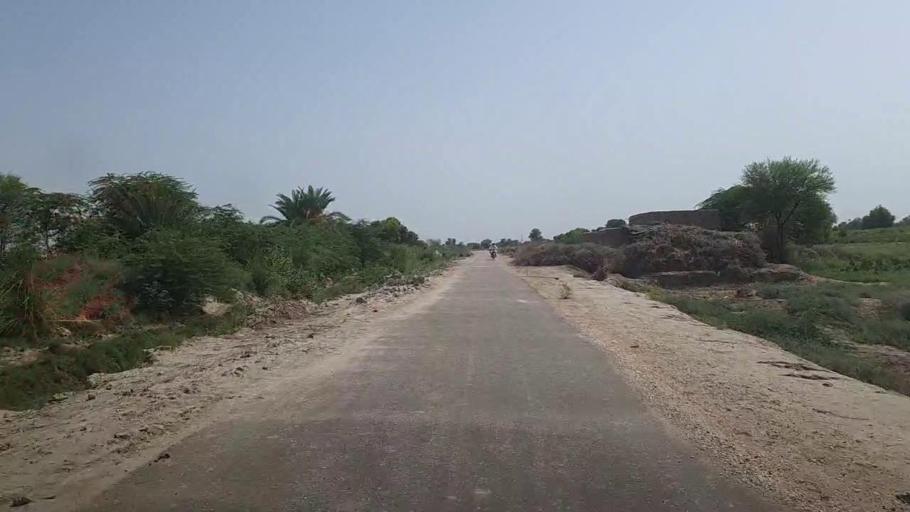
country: PK
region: Sindh
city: Pad Idan
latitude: 26.8290
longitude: 68.3301
